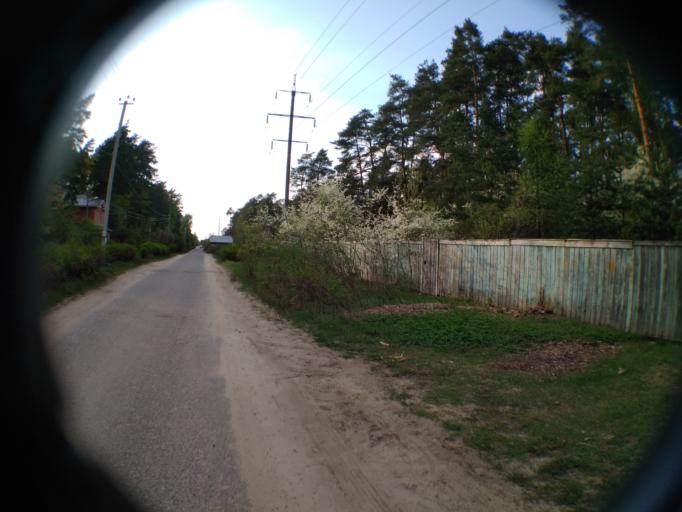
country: RU
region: Moskovskaya
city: Kratovo
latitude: 55.5805
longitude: 38.1645
